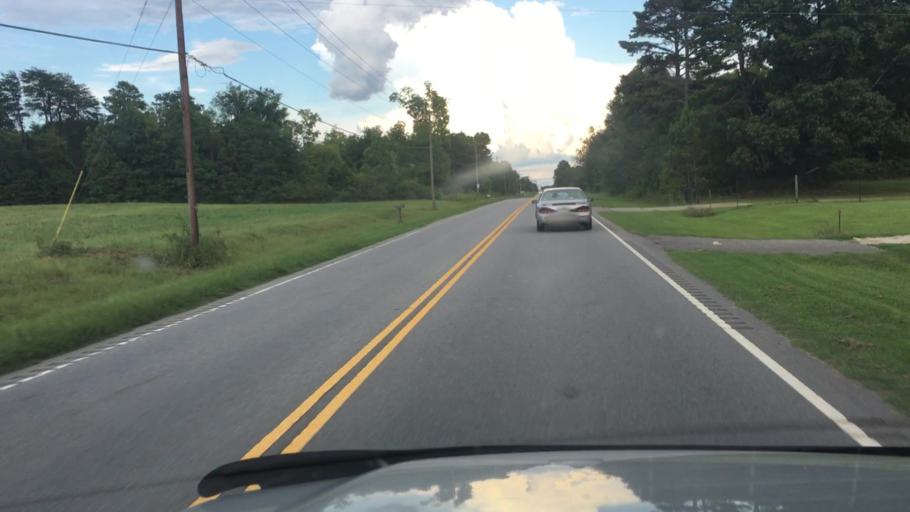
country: US
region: South Carolina
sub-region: Cherokee County
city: Gaffney
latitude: 35.1169
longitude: -81.7107
